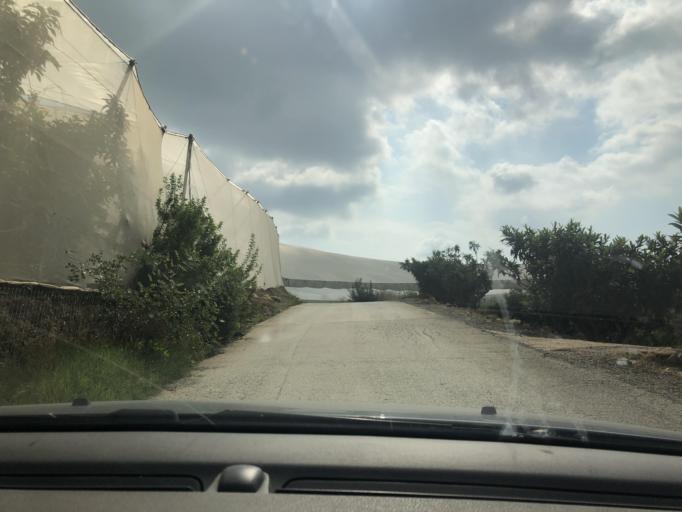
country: ES
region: Valencia
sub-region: Provincia de Alicante
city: Callosa d'En Sarria
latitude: 38.6543
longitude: -0.0902
